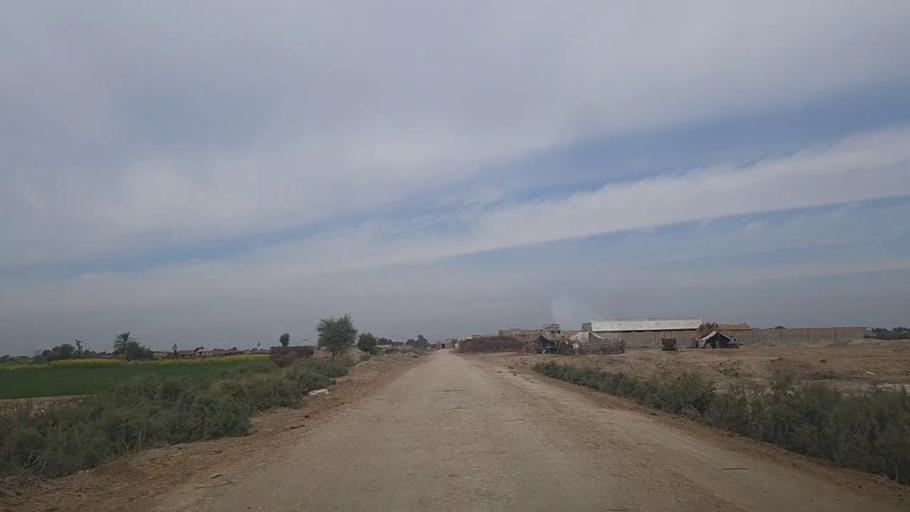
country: PK
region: Sindh
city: Sinjhoro
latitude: 26.1313
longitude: 68.8263
